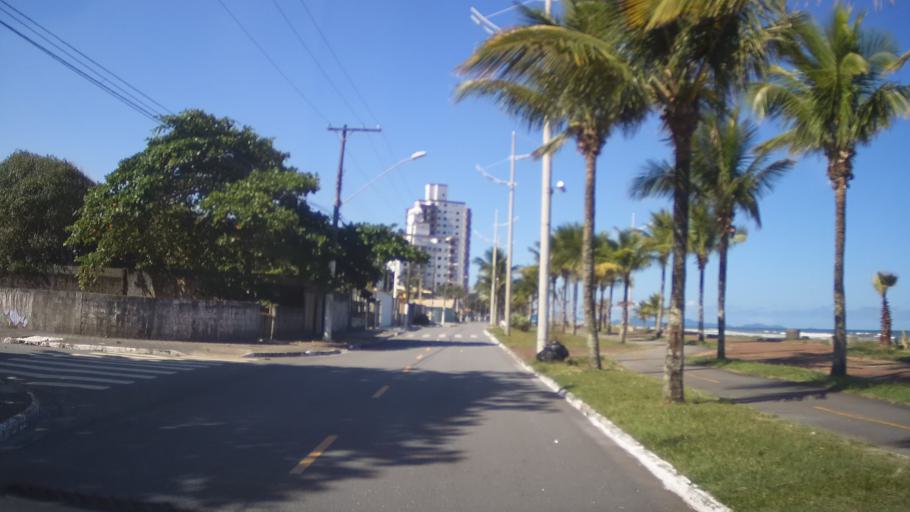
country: BR
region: Sao Paulo
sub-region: Mongagua
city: Mongagua
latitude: -24.0823
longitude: -46.5920
